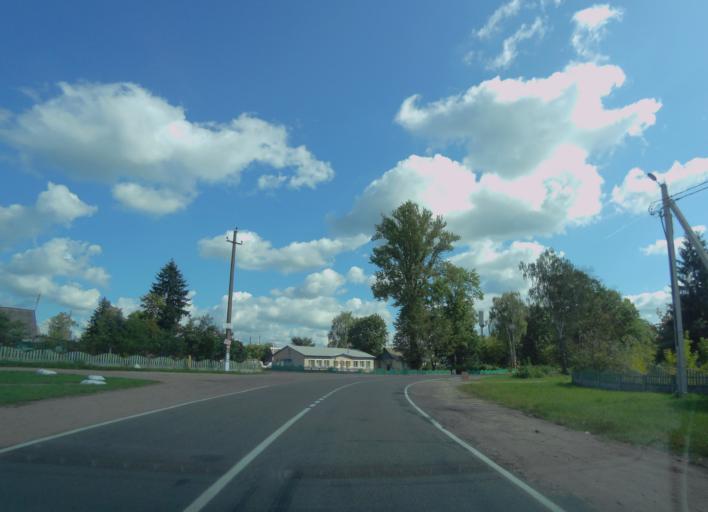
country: BY
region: Minsk
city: Zyembin
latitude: 54.3614
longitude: 28.3421
